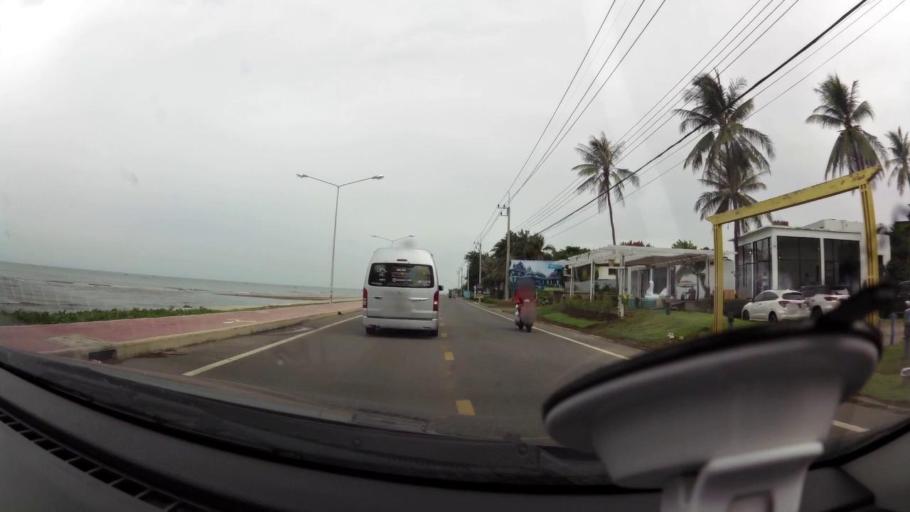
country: TH
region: Prachuap Khiri Khan
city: Pran Buri
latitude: 12.3943
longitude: 99.9961
